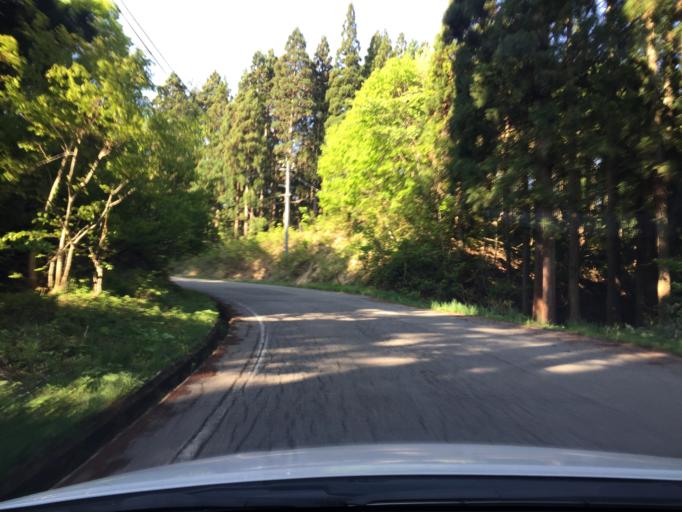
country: JP
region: Fukushima
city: Kitakata
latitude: 37.6874
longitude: 139.7010
